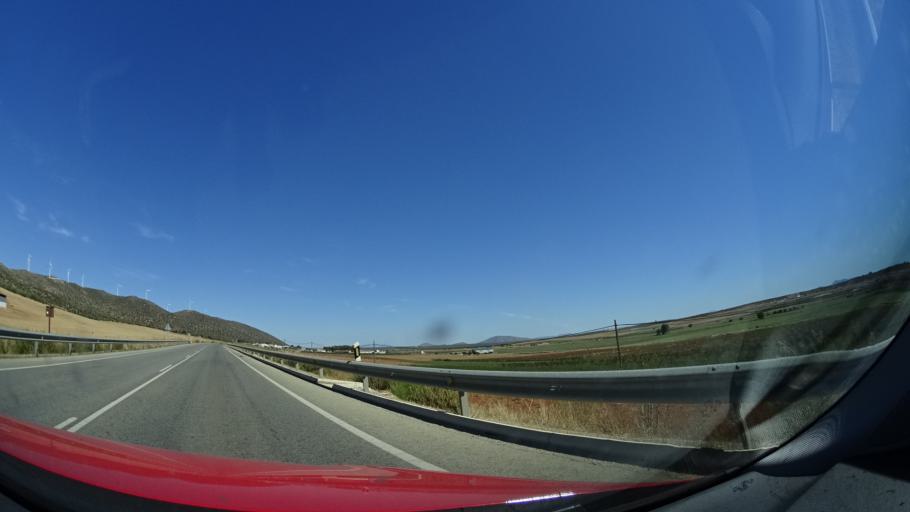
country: ES
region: Andalusia
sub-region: Provincia de Malaga
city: Sierra de Yeguas
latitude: 37.1499
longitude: -4.8541
